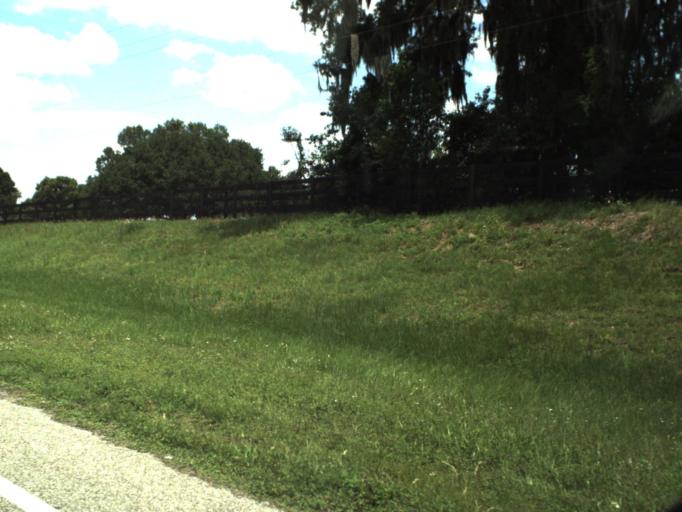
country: US
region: Florida
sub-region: Marion County
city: Citra
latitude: 29.3932
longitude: -82.1939
